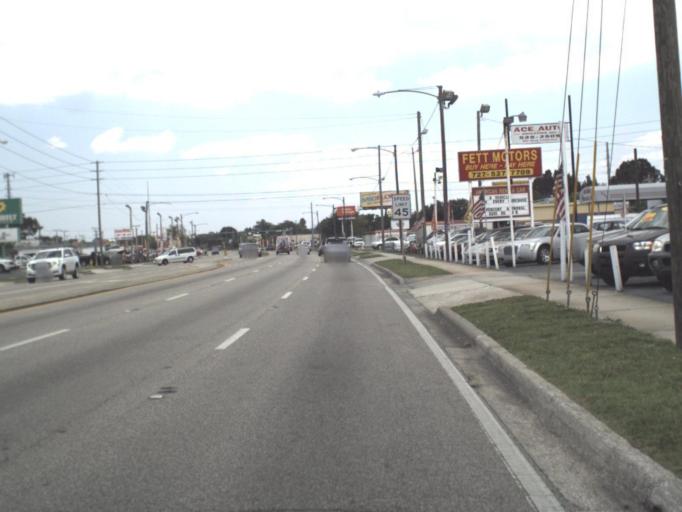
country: US
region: Florida
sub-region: Pinellas County
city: Lealman
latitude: 27.8291
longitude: -82.6795
